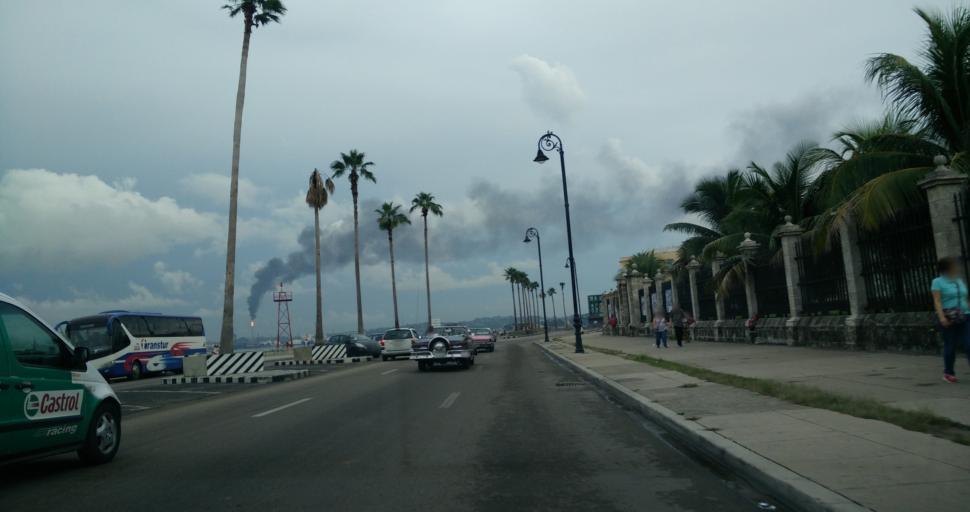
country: CU
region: La Habana
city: La Habana Vieja
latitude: 23.1419
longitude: -82.3499
